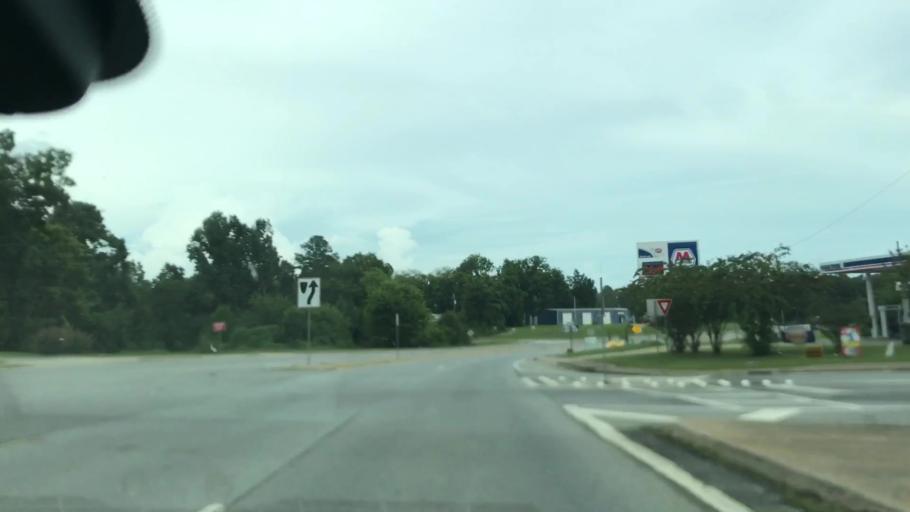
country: US
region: Georgia
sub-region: Quitman County
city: Georgetown
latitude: 31.8878
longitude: -85.1089
